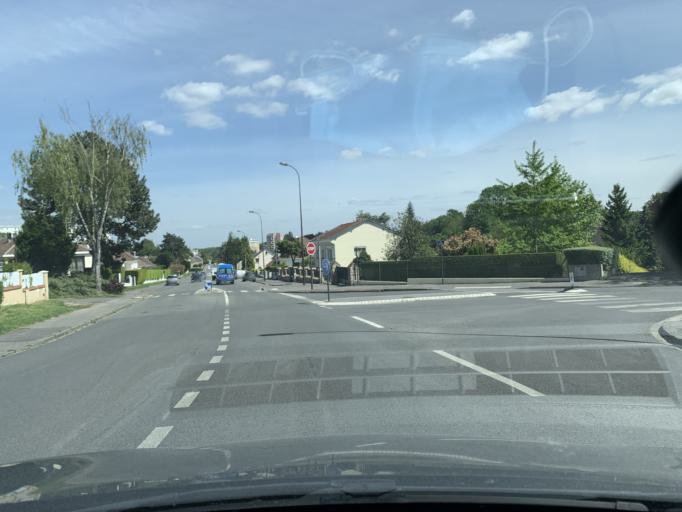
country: FR
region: Picardie
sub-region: Departement de l'Aisne
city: Saint-Quentin
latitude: 49.8583
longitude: 3.2963
